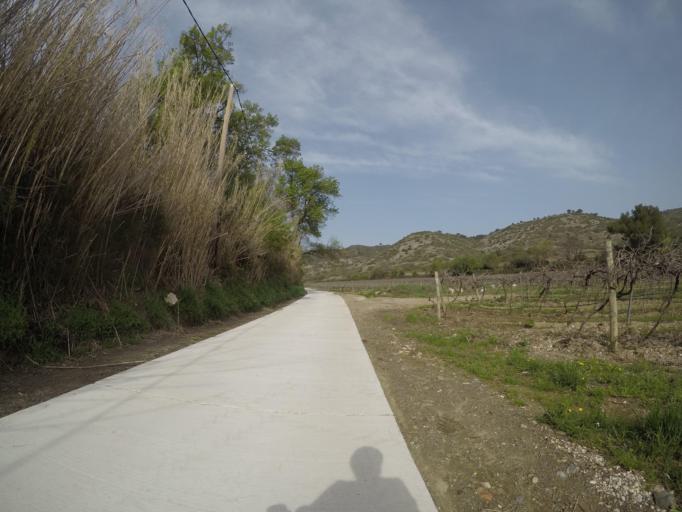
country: FR
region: Languedoc-Roussillon
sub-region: Departement des Pyrenees-Orientales
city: Estagel
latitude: 42.7778
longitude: 2.7316
